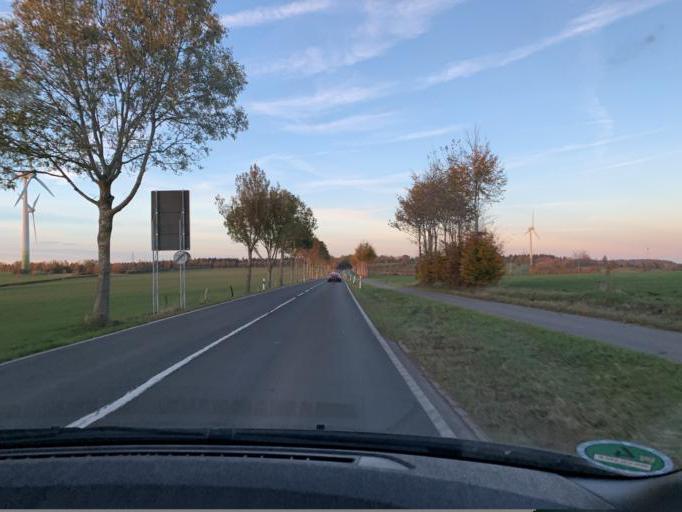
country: DE
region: North Rhine-Westphalia
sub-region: Regierungsbezirk Koln
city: Simmerath
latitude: 50.6367
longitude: 6.3436
